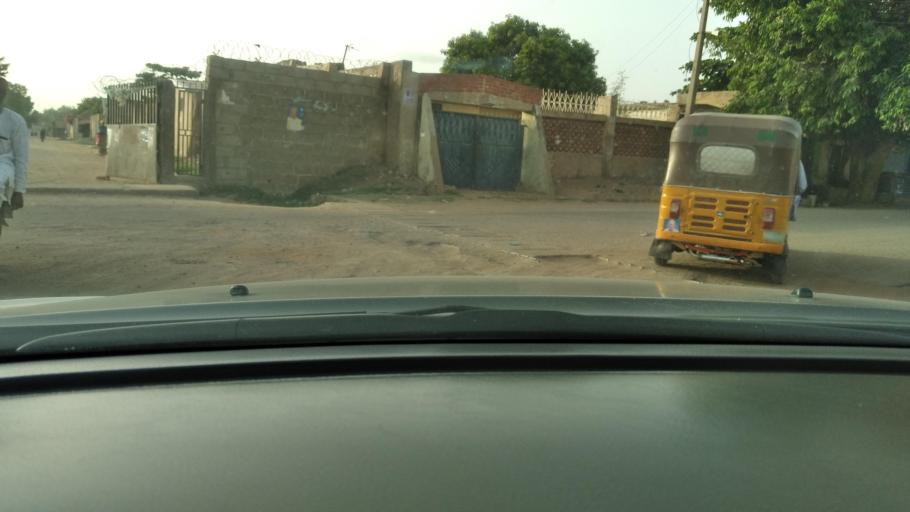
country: NG
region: Kano
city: Kano
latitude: 11.9516
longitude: 8.5214
